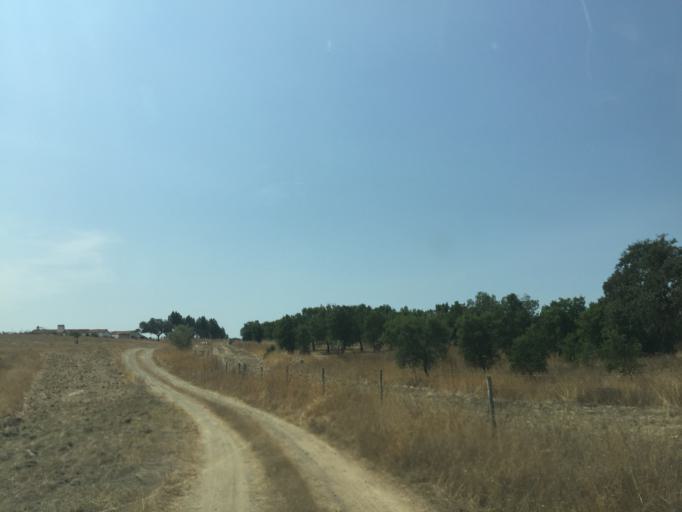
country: PT
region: Setubal
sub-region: Grandola
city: Grandola
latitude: 38.0527
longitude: -8.4513
